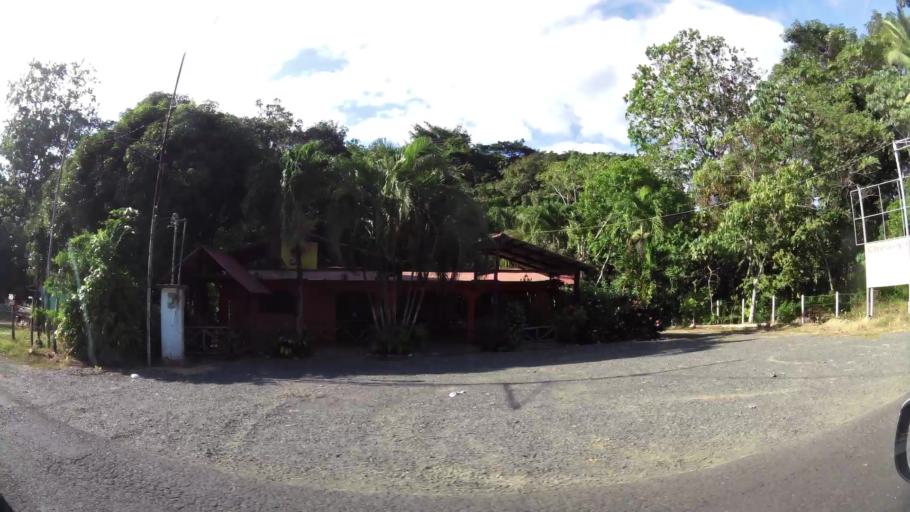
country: CR
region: Puntarenas
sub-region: Canton de Garabito
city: Jaco
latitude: 9.6548
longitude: -84.6488
